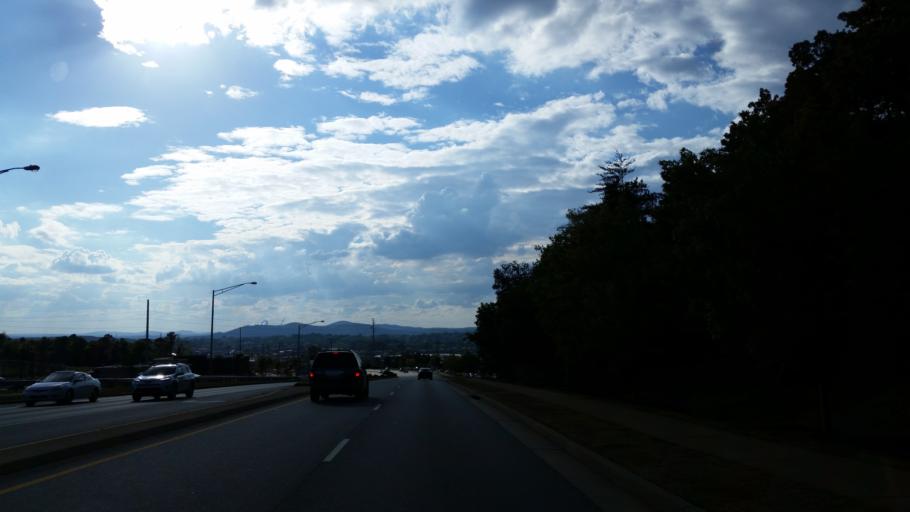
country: US
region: Georgia
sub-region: Bartow County
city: Cartersville
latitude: 34.1745
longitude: -84.7752
